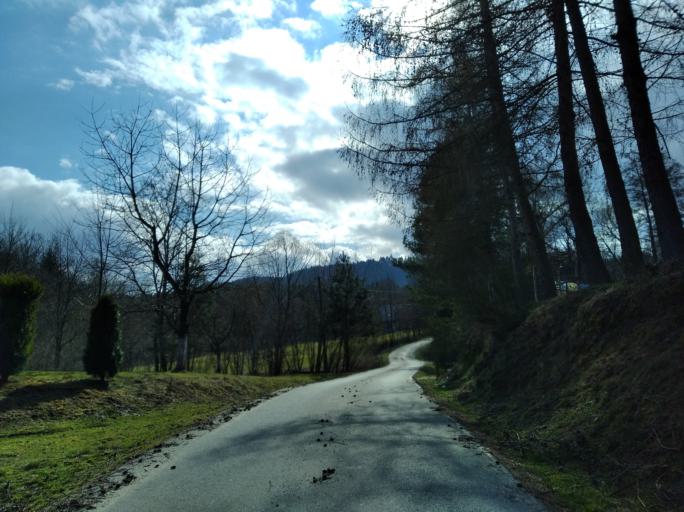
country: PL
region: Subcarpathian Voivodeship
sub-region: Powiat strzyzowski
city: Wysoka Strzyzowska
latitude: 49.8037
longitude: 21.7396
